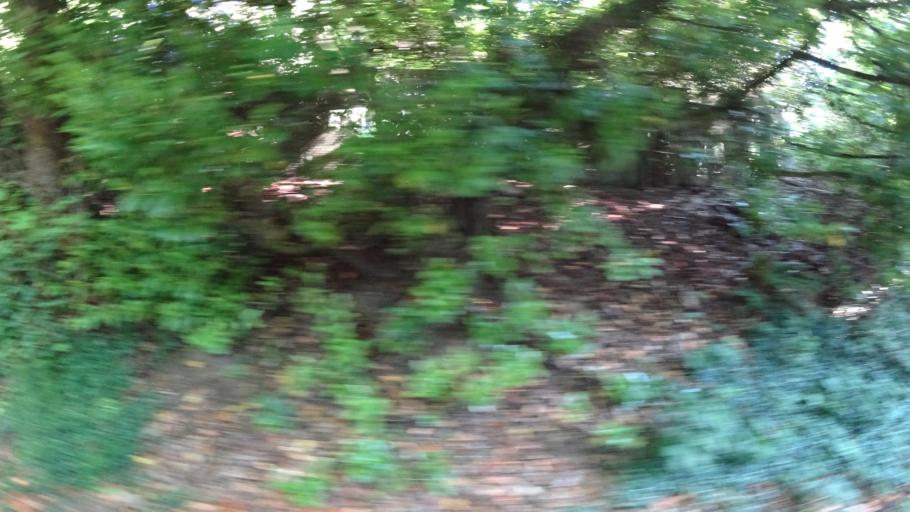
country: US
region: Oregon
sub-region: Washington County
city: West Slope
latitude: 45.5000
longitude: -122.7197
